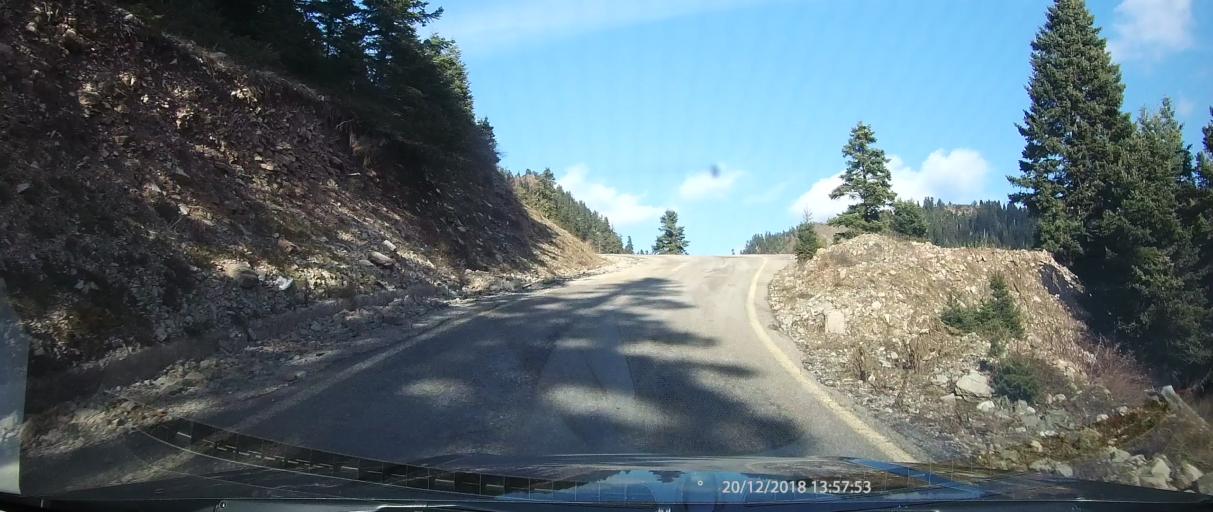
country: GR
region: West Greece
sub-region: Nomos Aitolias kai Akarnanias
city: Thermo
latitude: 38.7128
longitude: 21.6218
